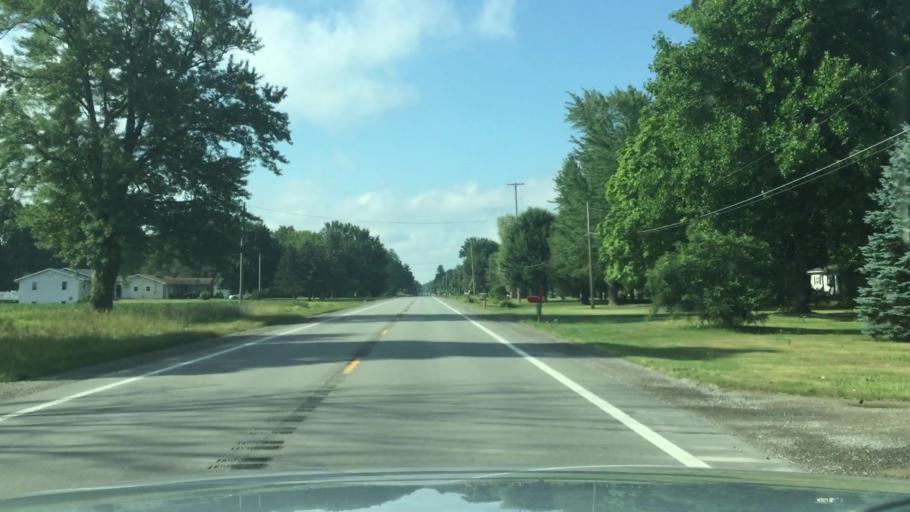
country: US
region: Michigan
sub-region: Saginaw County
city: Birch Run
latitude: 43.2408
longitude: -83.7354
